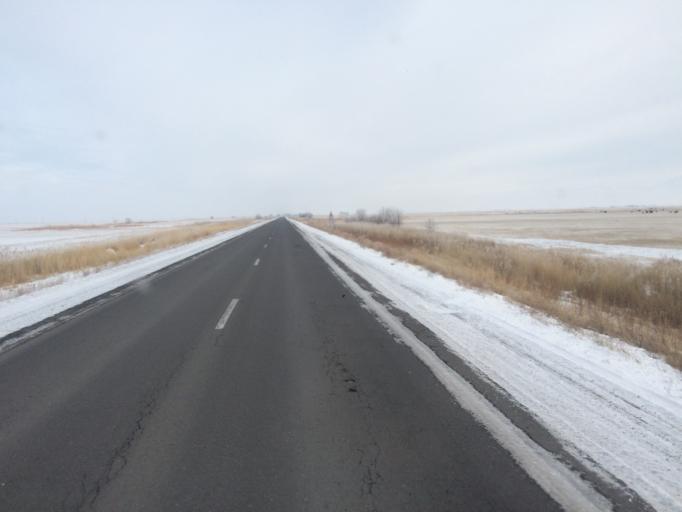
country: KG
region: Chuy
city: Tokmok
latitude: 43.3549
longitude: 75.4348
